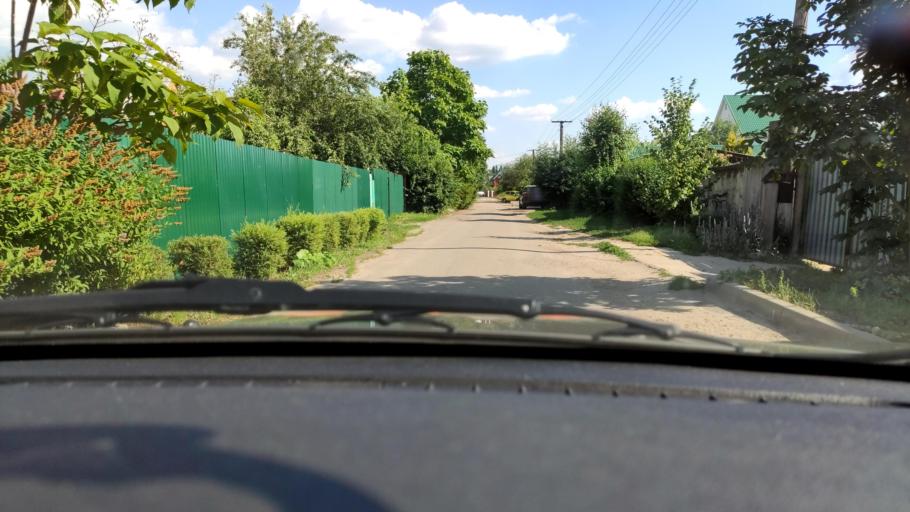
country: RU
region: Voronezj
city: Ramon'
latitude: 51.8313
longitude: 39.2676
